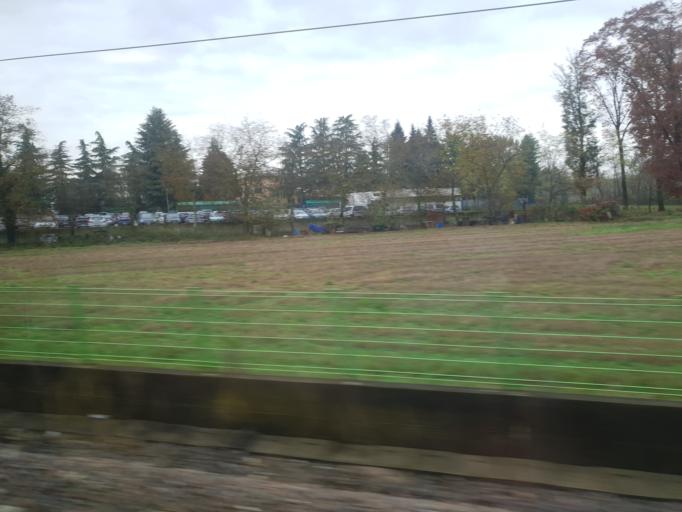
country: IT
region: Lombardy
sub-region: Citta metropolitana di Milano
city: Rescaldina
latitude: 45.6237
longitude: 8.9645
